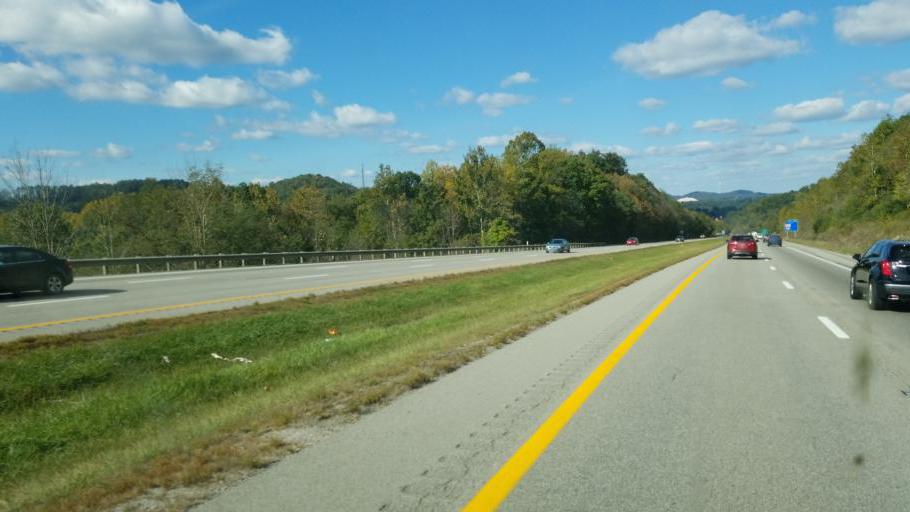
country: US
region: West Virginia
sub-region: Monongalia County
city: Westover
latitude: 39.6114
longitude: -79.9926
